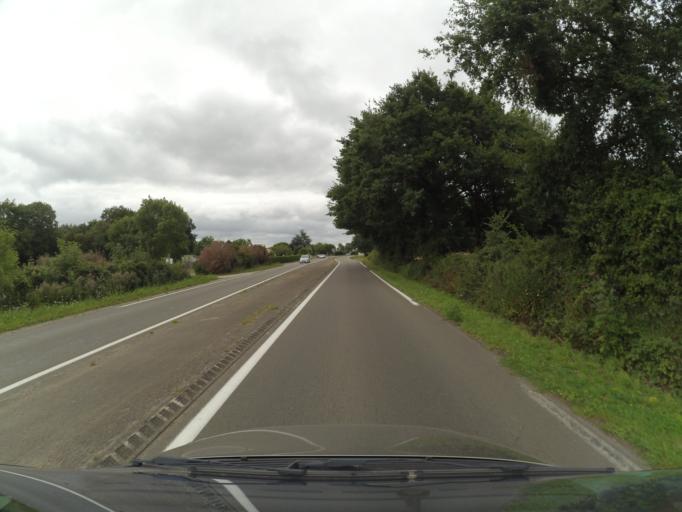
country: FR
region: Pays de la Loire
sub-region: Departement de la Vendee
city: La Boissiere-des-Landes
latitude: 46.5615
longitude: -1.4505
